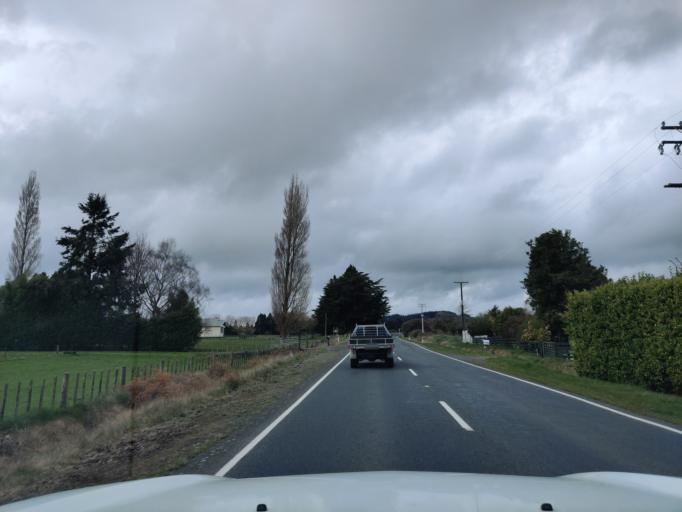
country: NZ
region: Manawatu-Wanganui
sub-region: Ruapehu District
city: Waiouru
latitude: -39.3699
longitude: 175.3143
